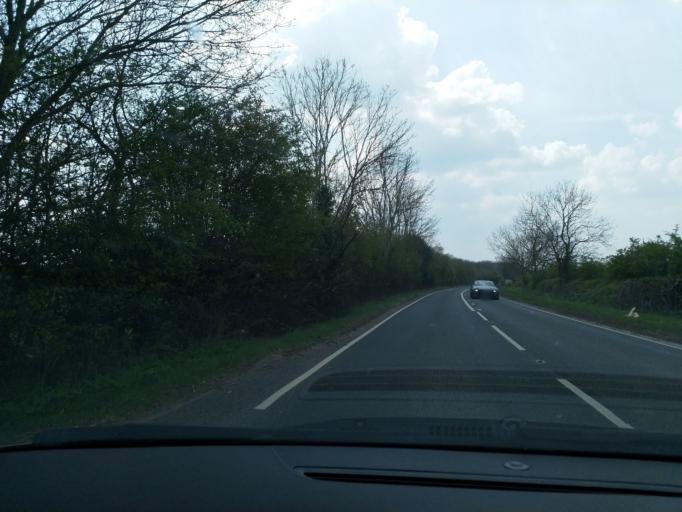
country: GB
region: England
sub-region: Warwickshire
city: Ryton on Dunsmore
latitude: 52.3512
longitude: -1.4550
